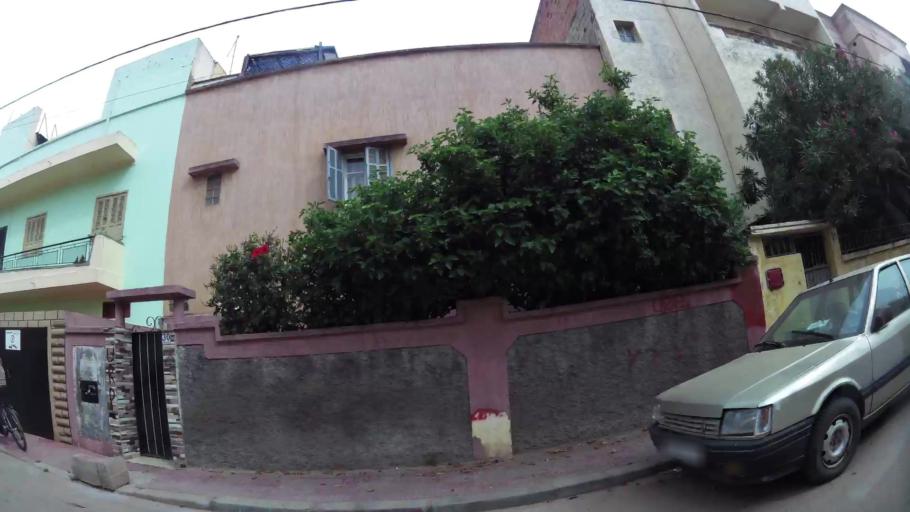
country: MA
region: Rabat-Sale-Zemmour-Zaer
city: Sale
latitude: 34.0435
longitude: -6.8088
